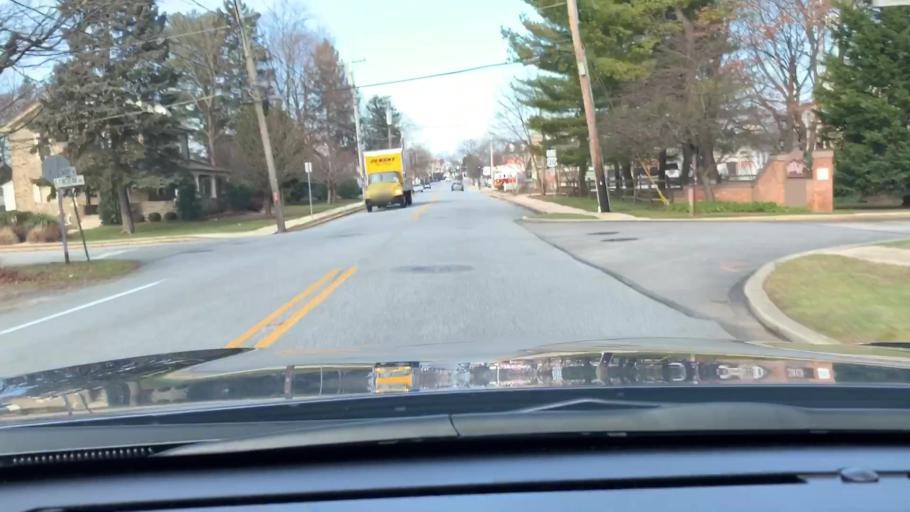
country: US
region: Pennsylvania
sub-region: Chester County
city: Paoli
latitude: 40.0393
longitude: -75.4806
